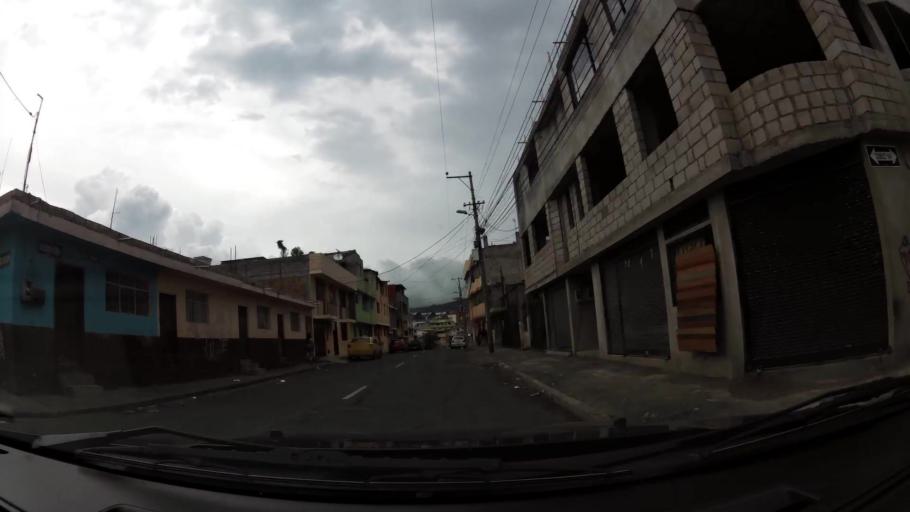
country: EC
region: Pichincha
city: Quito
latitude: -0.2860
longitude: -78.5394
